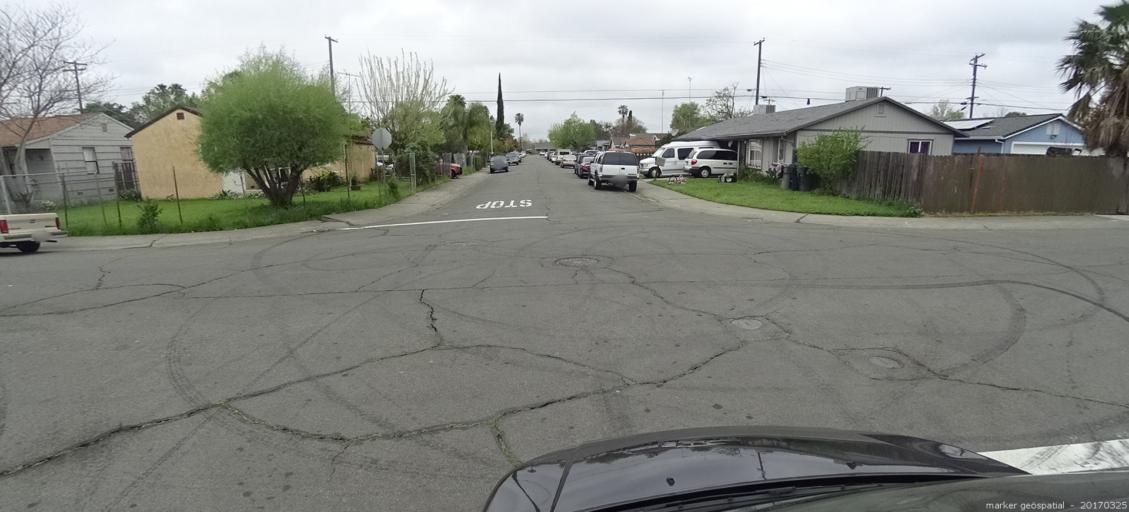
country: US
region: California
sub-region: Sacramento County
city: Florin
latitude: 38.5205
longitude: -121.4117
